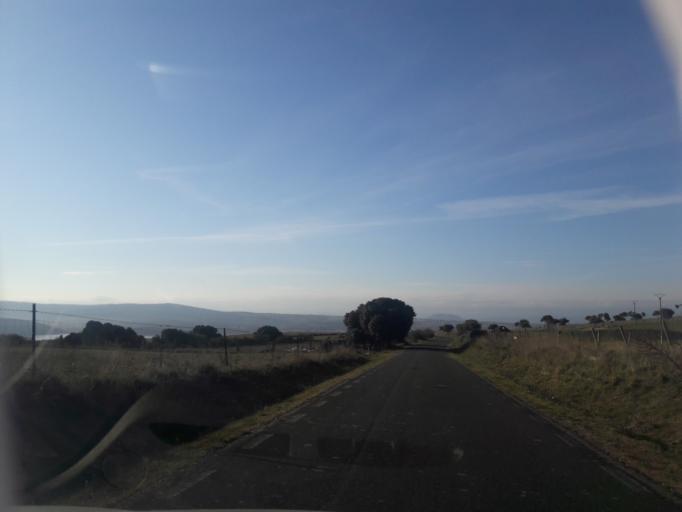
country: ES
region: Castille and Leon
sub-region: Provincia de Salamanca
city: Salvatierra de Tormes
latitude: 40.6069
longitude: -5.6015
